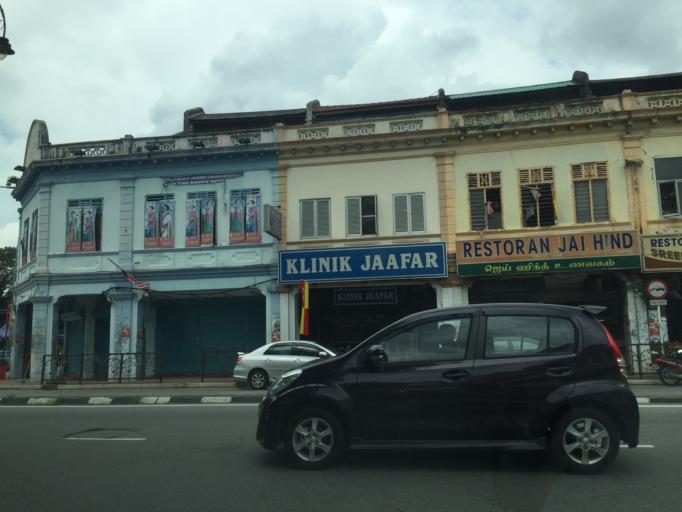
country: MY
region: Selangor
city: Klang
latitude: 3.0395
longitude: 101.4467
